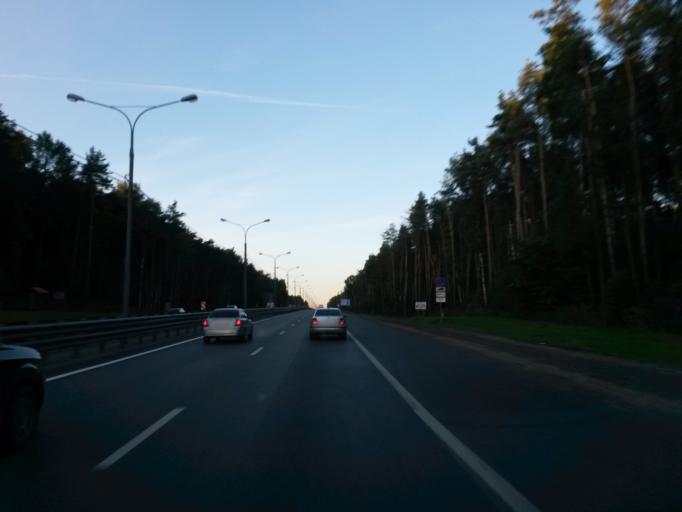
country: RU
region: Moskovskaya
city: Kostino
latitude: 56.0408
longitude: 37.8924
